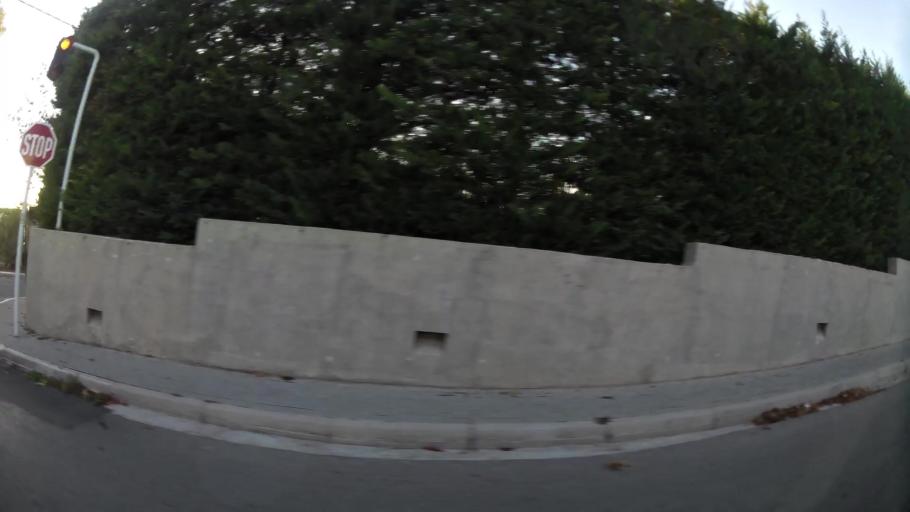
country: GR
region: Attica
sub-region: Nomarchia Anatolikis Attikis
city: Kryoneri
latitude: 38.1410
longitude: 23.8373
